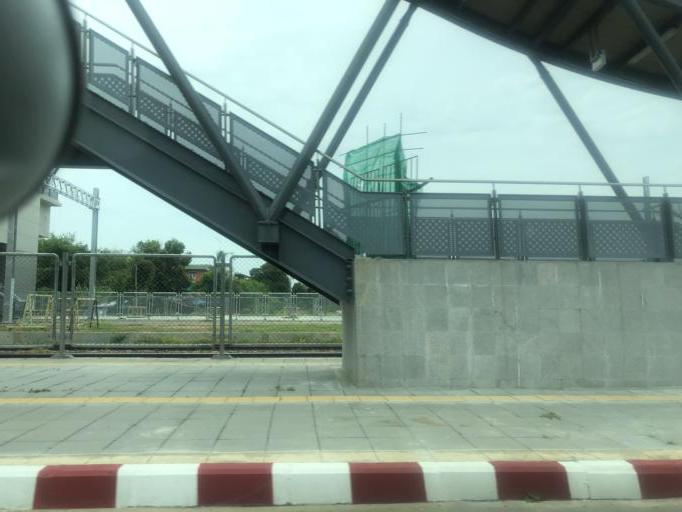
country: TH
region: Bangkok
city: Don Mueang
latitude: 13.9647
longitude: 100.6052
